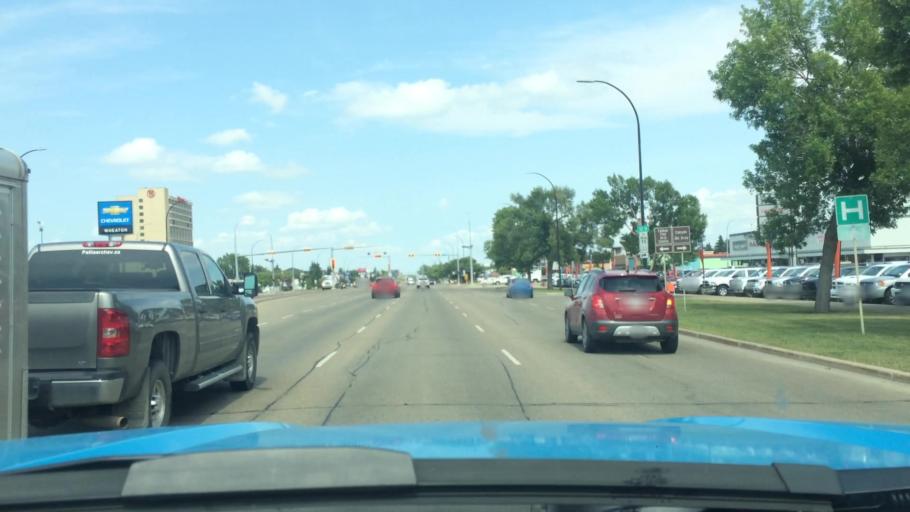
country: CA
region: Alberta
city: Red Deer
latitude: 52.2493
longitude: -113.8139
